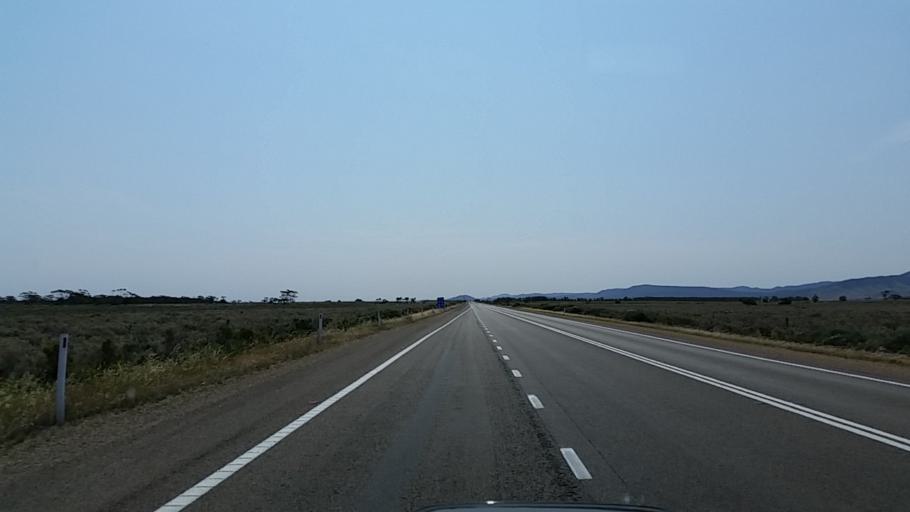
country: AU
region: South Australia
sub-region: Port Pirie City and Dists
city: Port Pirie
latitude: -32.9710
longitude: 137.9825
